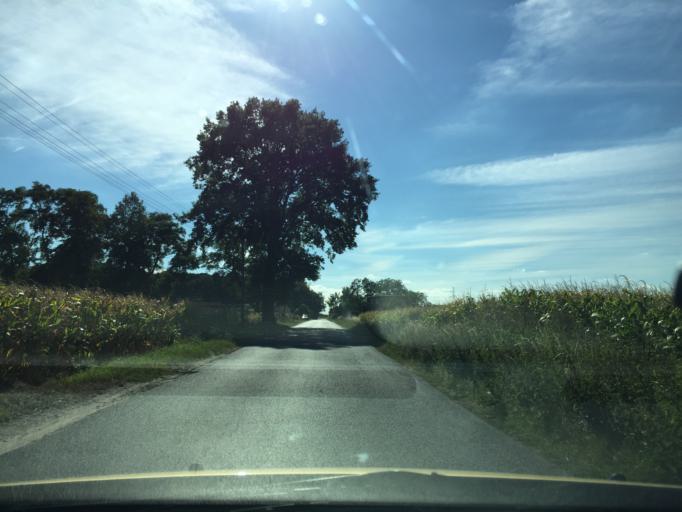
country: PL
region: Greater Poland Voivodeship
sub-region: Powiat kaliski
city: Stawiszyn
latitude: 51.9450
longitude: 18.1549
